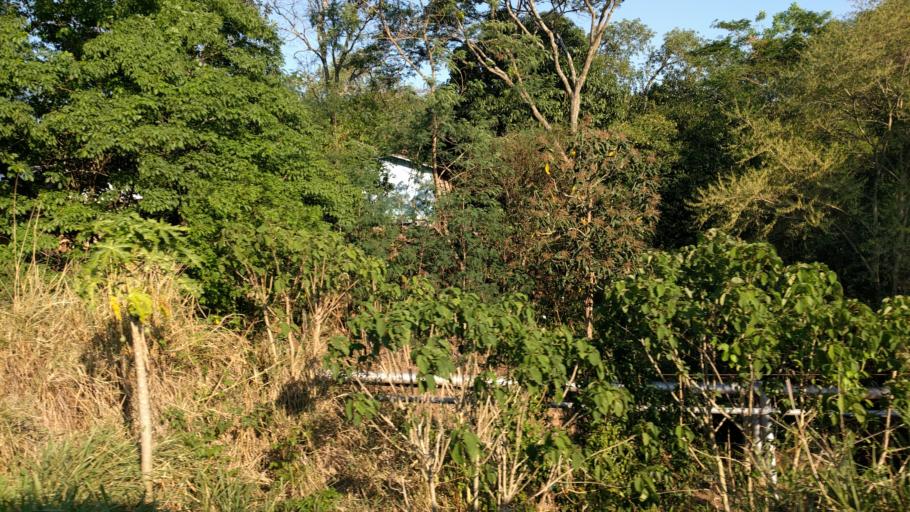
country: BO
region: Santa Cruz
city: Jorochito
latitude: -18.0682
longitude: -63.4387
